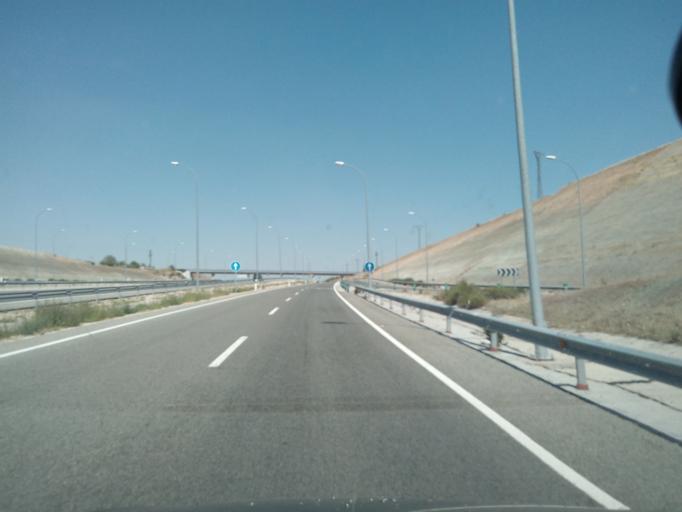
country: ES
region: Madrid
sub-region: Provincia de Madrid
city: Paracuellos de Jarama
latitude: 40.4648
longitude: -3.5132
